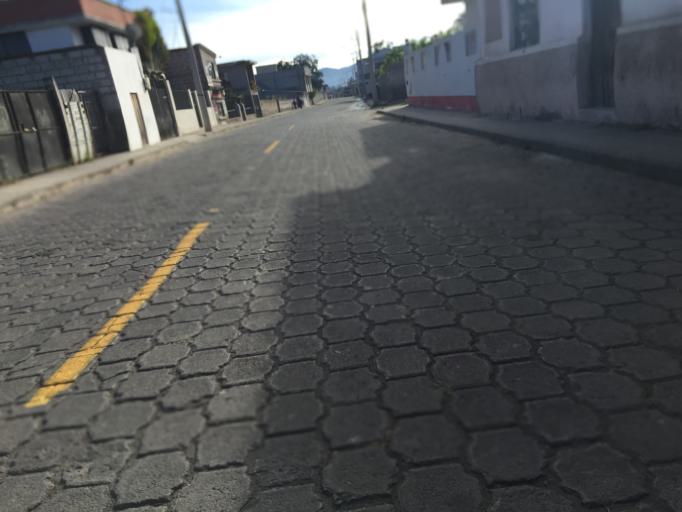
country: EC
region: Imbabura
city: Atuntaqui
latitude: 0.3376
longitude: -78.1968
